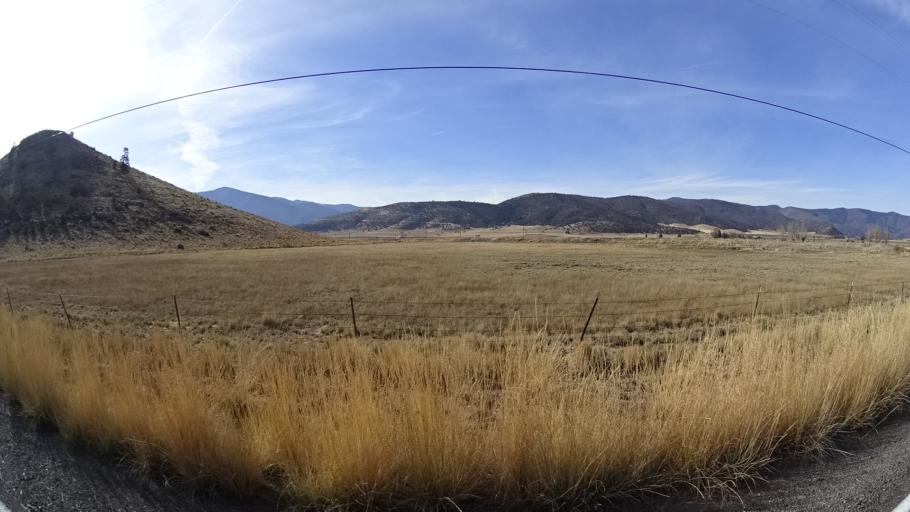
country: US
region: California
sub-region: Siskiyou County
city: Weed
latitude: 41.5375
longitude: -122.5223
